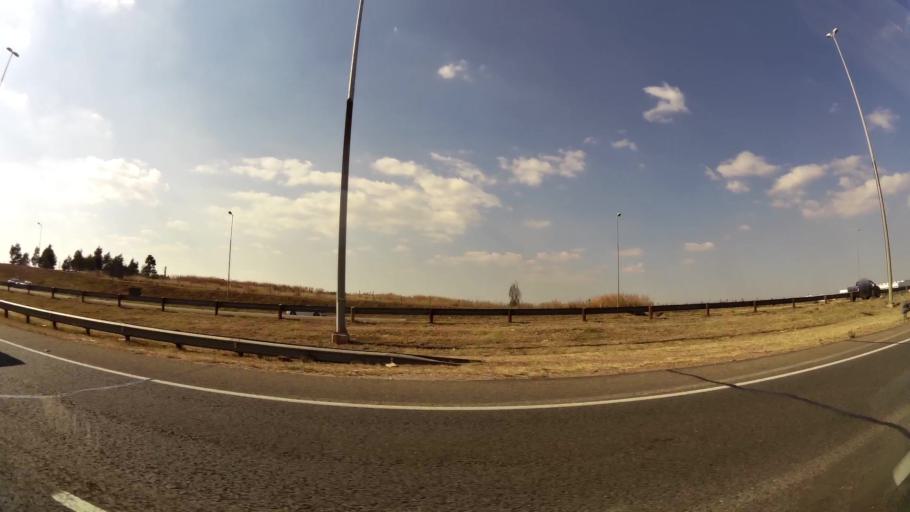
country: ZA
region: Gauteng
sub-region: Ekurhuleni Metropolitan Municipality
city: Tembisa
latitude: -26.0664
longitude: 28.2760
